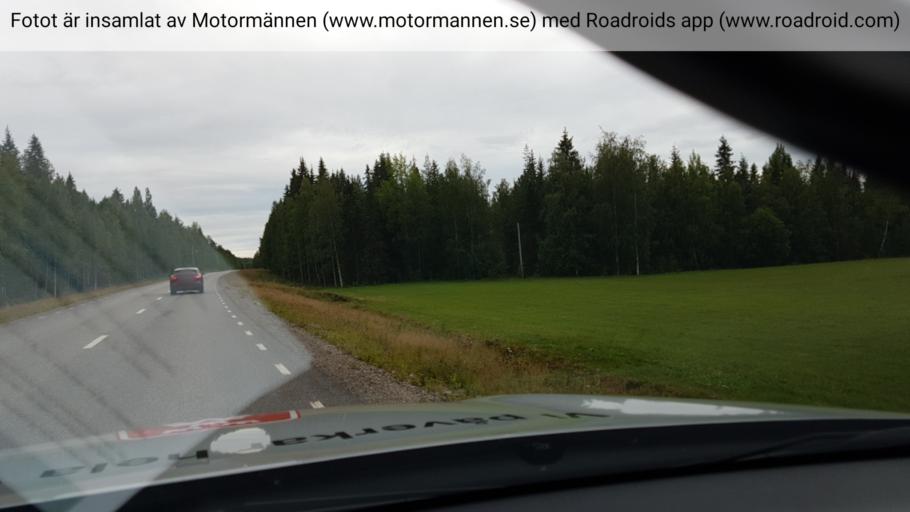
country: SE
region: Norrbotten
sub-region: Overkalix Kommun
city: OEverkalix
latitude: 66.5660
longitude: 22.7615
